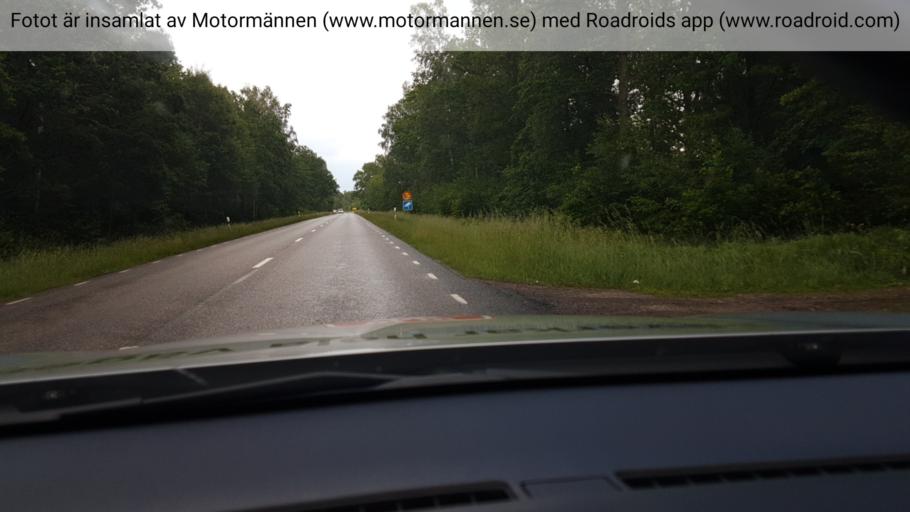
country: SE
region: Vaestra Goetaland
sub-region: Hjo Kommun
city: Hjo
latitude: 58.2601
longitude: 14.2493
